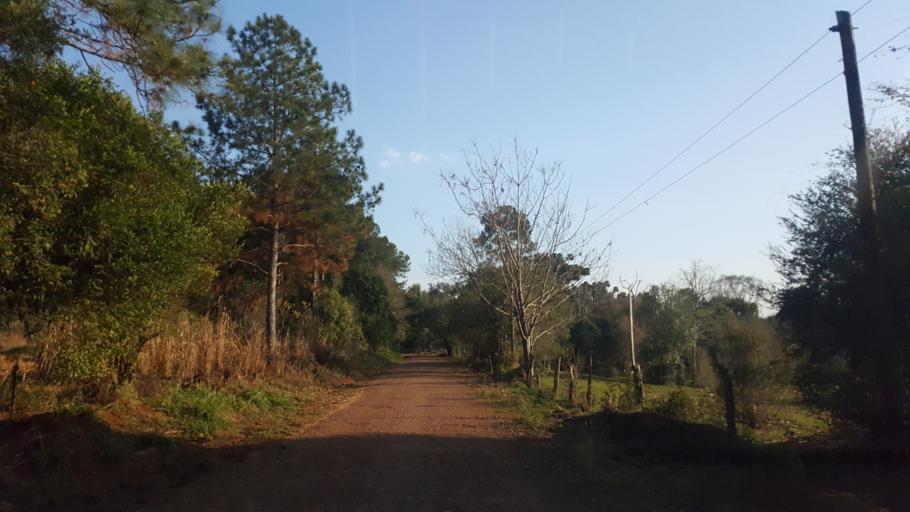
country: AR
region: Misiones
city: Capiovi
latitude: -26.9007
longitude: -55.0547
